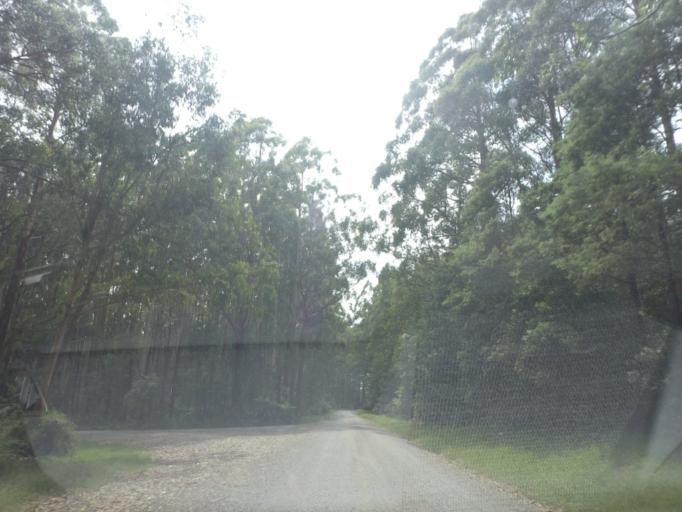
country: AU
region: Victoria
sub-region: Yarra Ranges
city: Healesville
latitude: -37.5058
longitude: 145.5276
